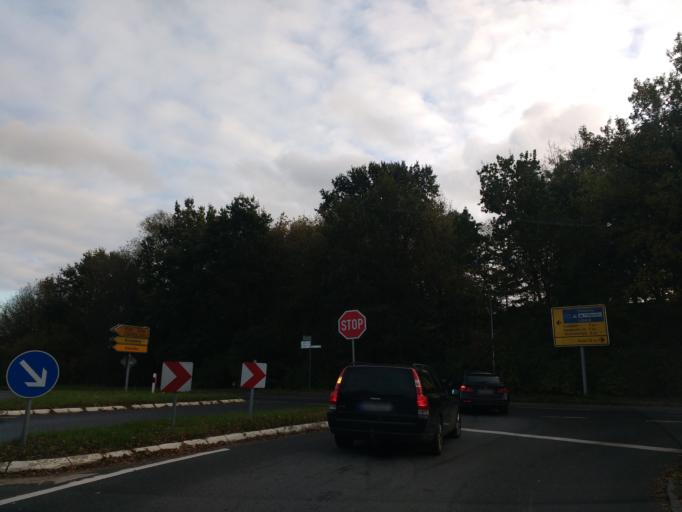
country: DE
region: Schleswig-Holstein
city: Schonwalde am Bungsberg
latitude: 54.1873
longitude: 10.7600
